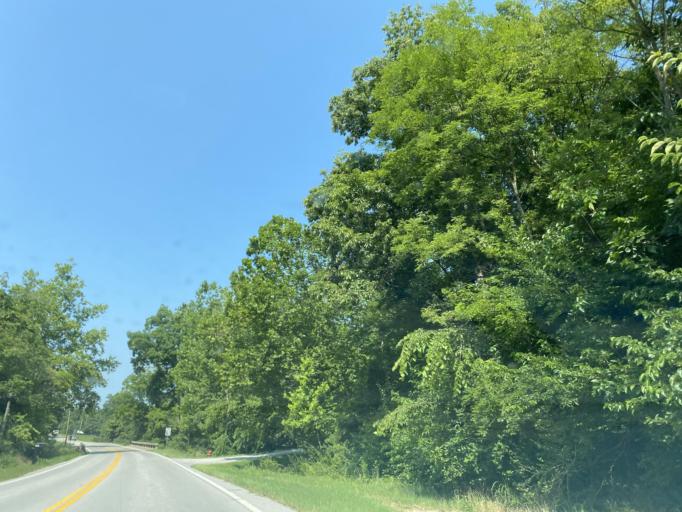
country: US
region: Kentucky
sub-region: Campbell County
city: Claryville
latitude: 38.9277
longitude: -84.4311
